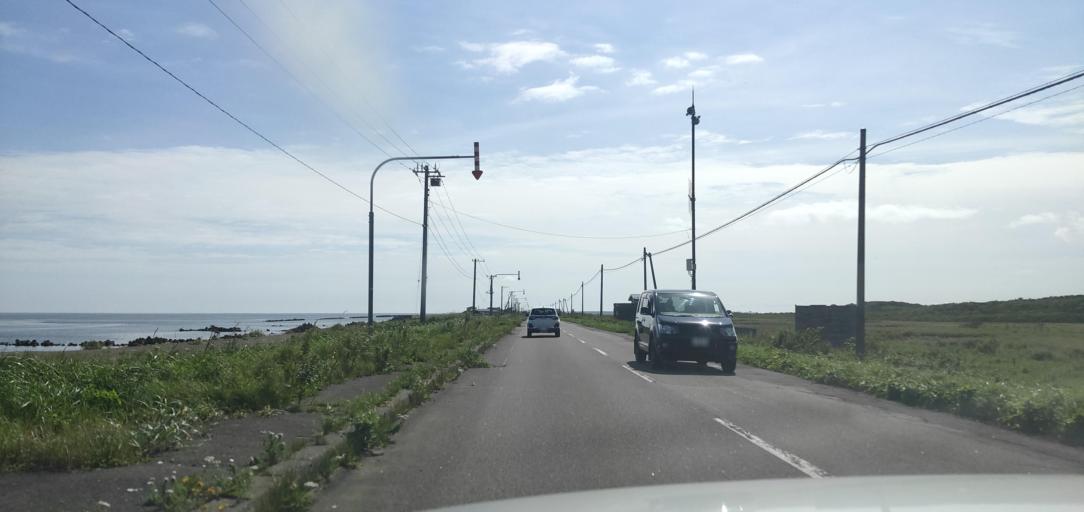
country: JP
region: Hokkaido
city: Shibetsu
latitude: 43.6346
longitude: 145.1771
